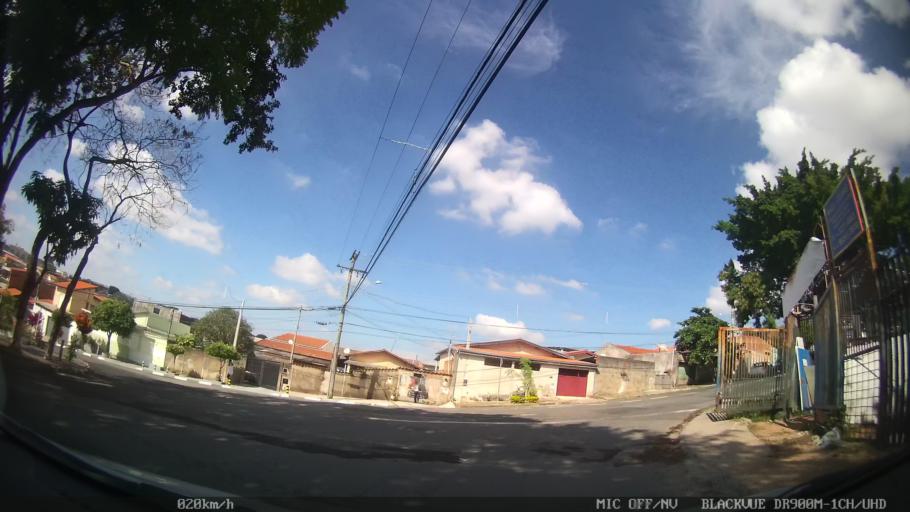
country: BR
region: Sao Paulo
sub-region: Campinas
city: Campinas
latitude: -22.9370
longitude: -47.1114
